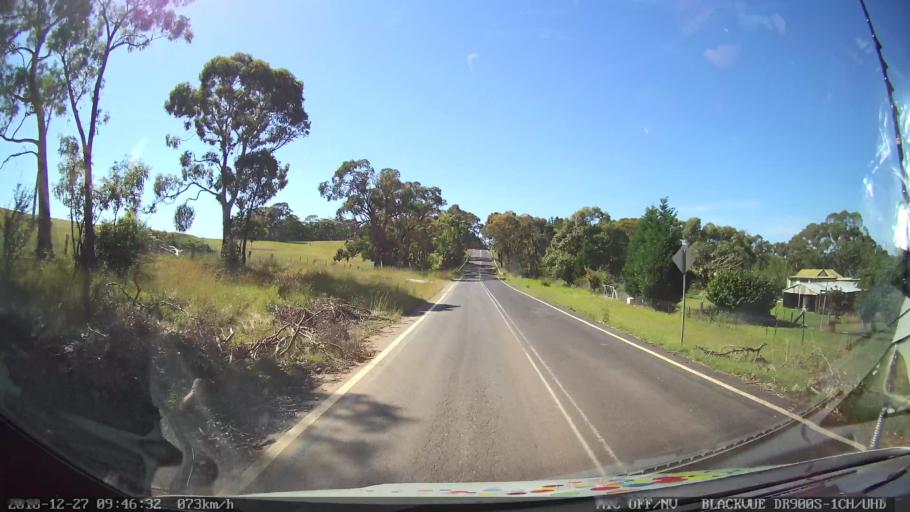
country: AU
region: New South Wales
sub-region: Lithgow
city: Portland
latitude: -33.3365
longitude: 149.9863
